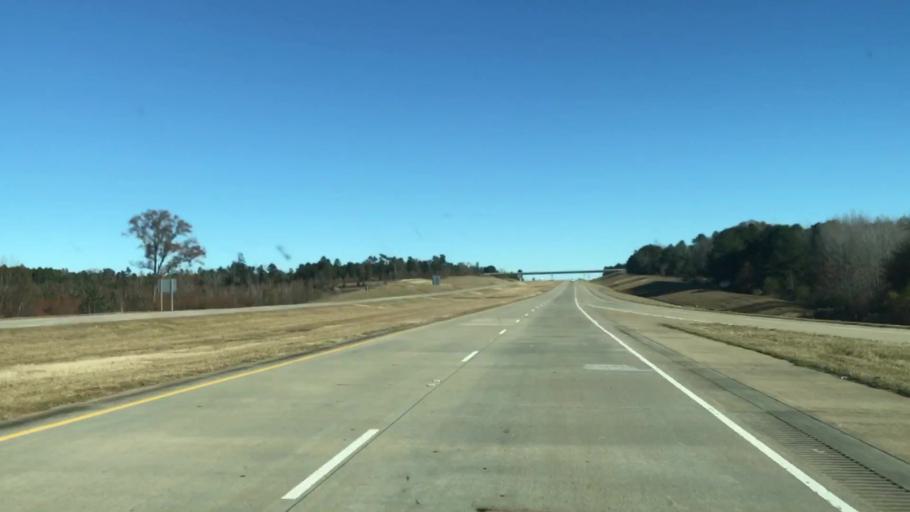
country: US
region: Louisiana
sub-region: Caddo Parish
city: Vivian
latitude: 33.0009
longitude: -93.9079
